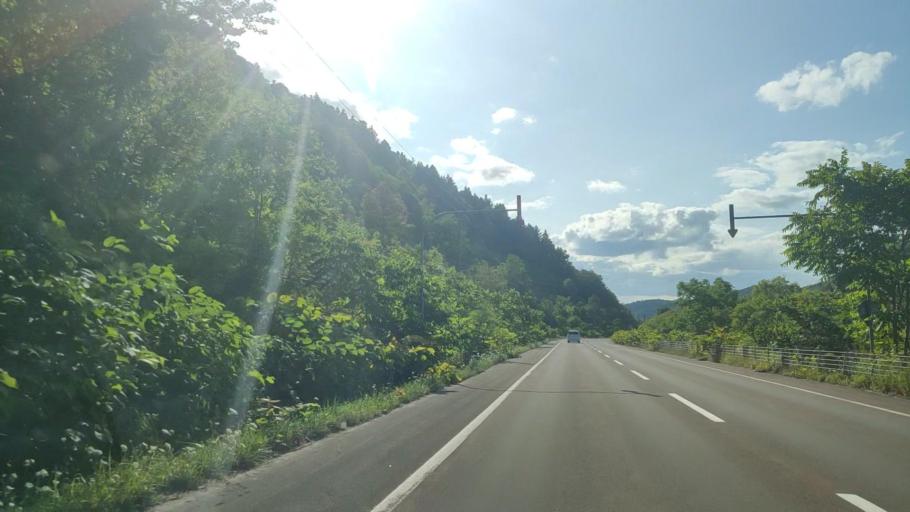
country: JP
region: Hokkaido
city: Nayoro
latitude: 44.7299
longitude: 142.1005
